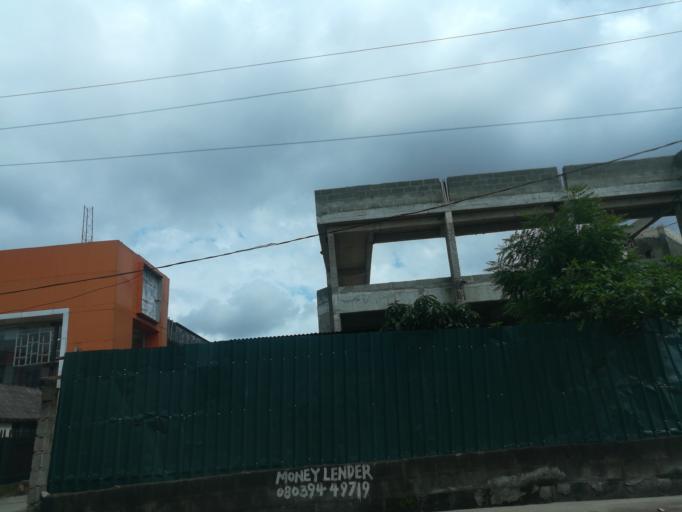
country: NG
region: Lagos
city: Somolu
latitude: 6.5456
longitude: 3.3598
